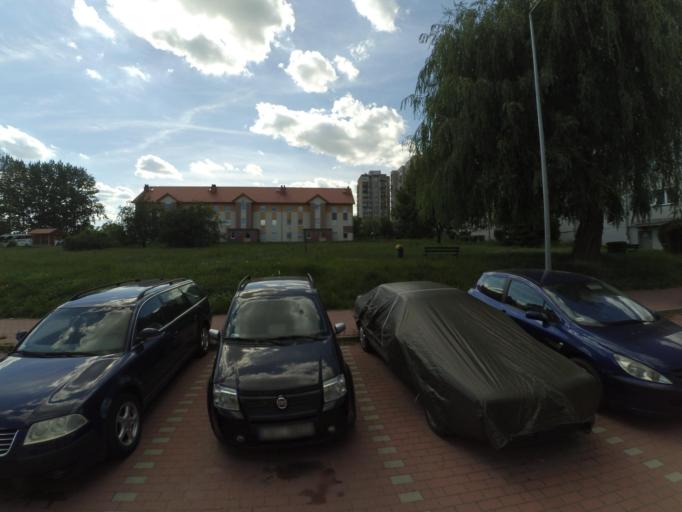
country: PL
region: Lower Silesian Voivodeship
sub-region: Powiat klodzki
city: Klodzko
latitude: 50.4317
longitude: 16.6431
